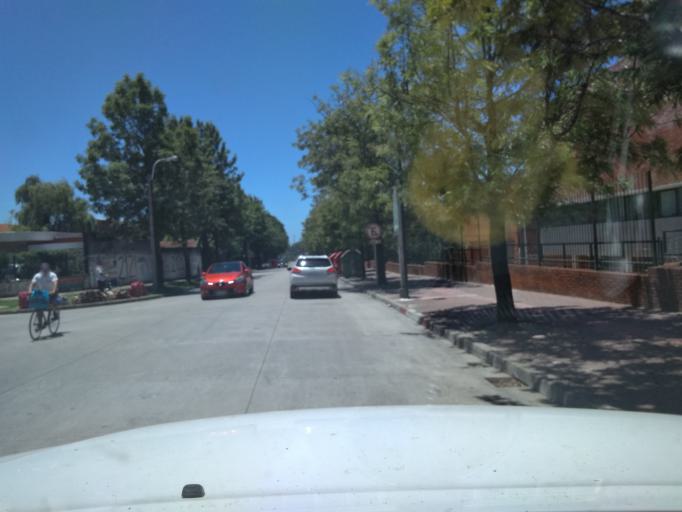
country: UY
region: Canelones
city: Paso de Carrasco
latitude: -34.8810
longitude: -56.0823
